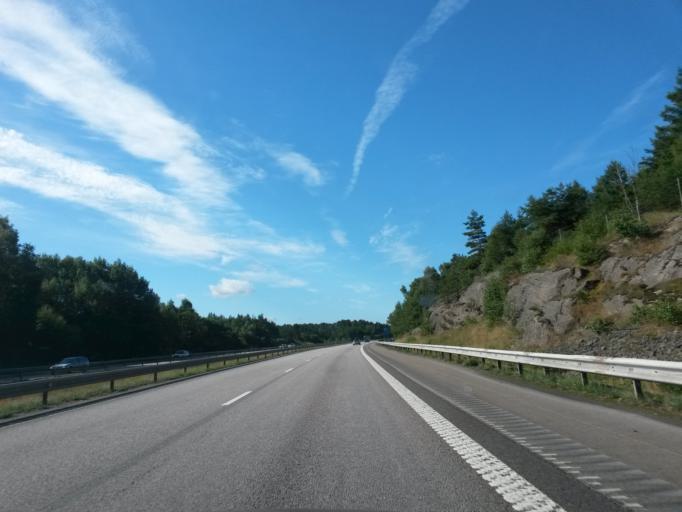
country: SE
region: Halland
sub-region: Kungsbacka Kommun
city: Frillesas
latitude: 57.3527
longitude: 12.2096
